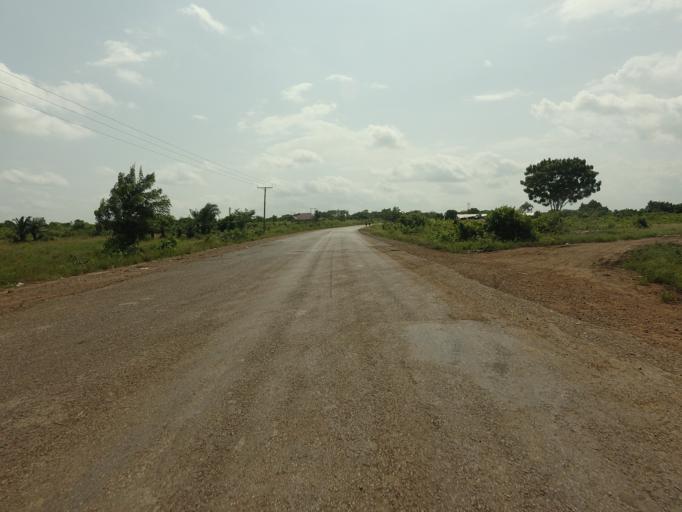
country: TG
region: Maritime
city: Lome
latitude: 6.2482
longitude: 0.9757
